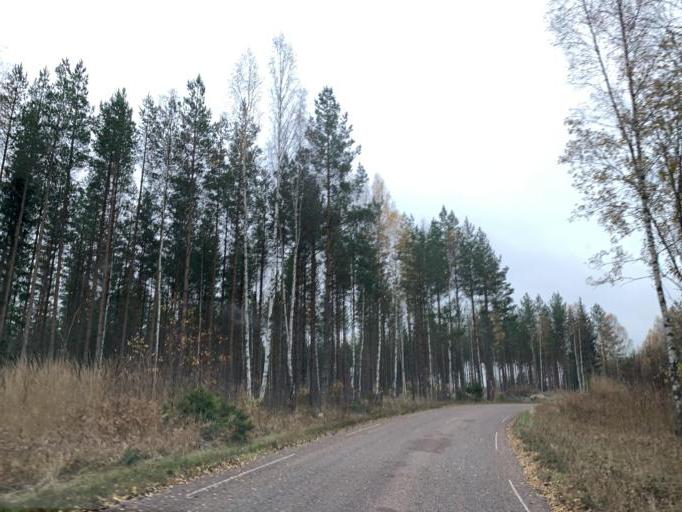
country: SE
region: Vaestmanland
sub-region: Surahammars Kommun
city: Surahammar
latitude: 59.6693
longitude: 16.0808
